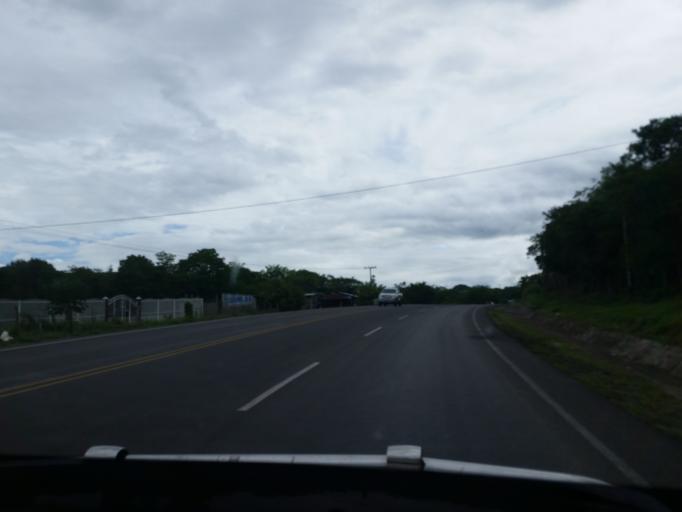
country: NI
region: Matagalpa
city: Ciudad Dario
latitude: 12.8840
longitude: -86.0787
